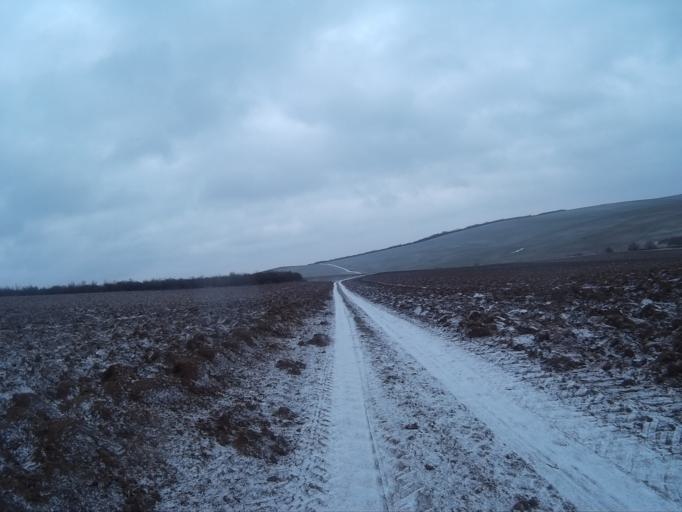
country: HU
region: Borsod-Abauj-Zemplen
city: Halmaj
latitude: 48.3648
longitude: 20.9255
